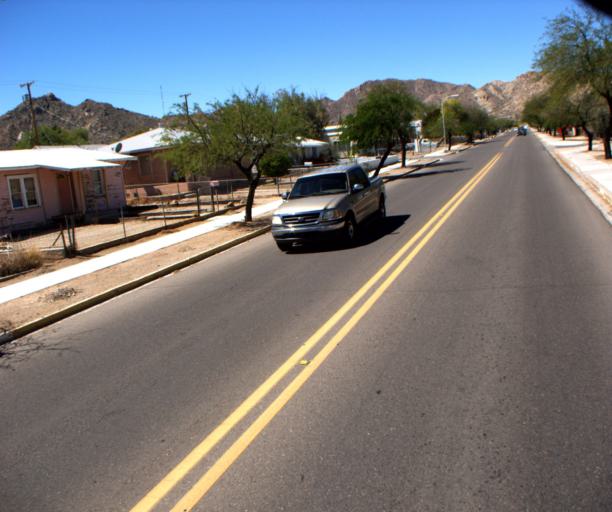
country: US
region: Arizona
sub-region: Pima County
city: Ajo
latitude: 32.3749
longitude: -112.8664
